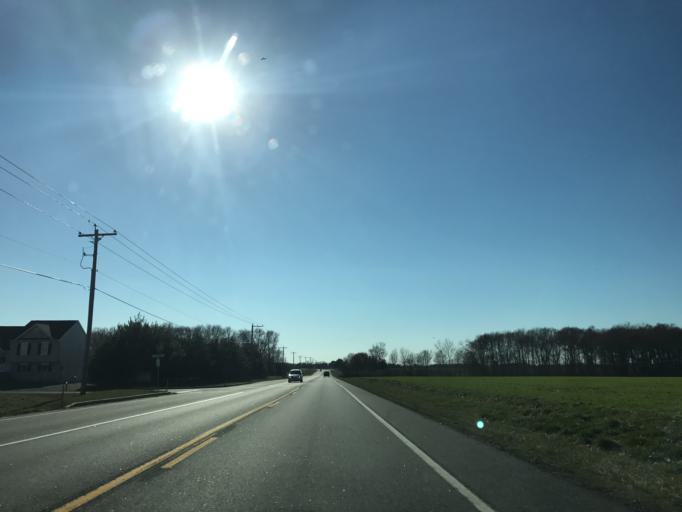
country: US
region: Maryland
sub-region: Caroline County
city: Ridgely
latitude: 39.0313
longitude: -75.8928
